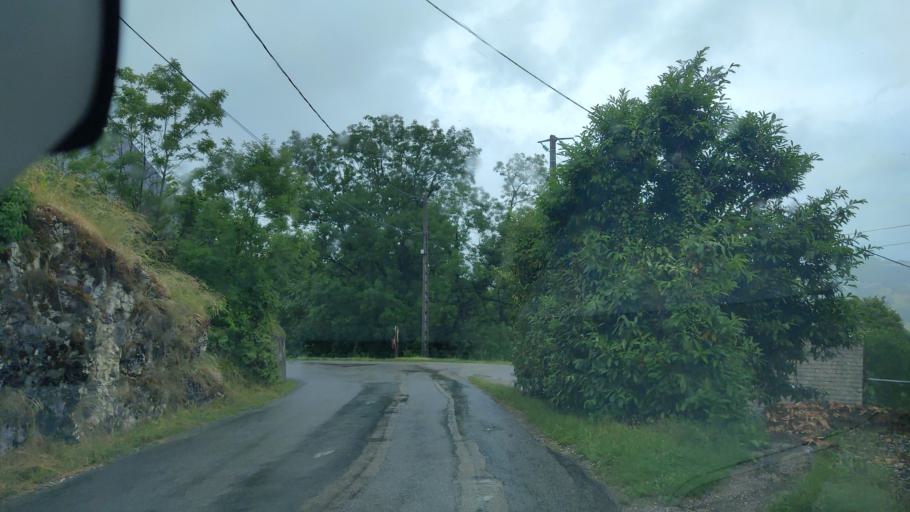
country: FR
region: Rhone-Alpes
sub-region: Departement de la Savoie
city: Chatillon
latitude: 45.7773
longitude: 5.8754
